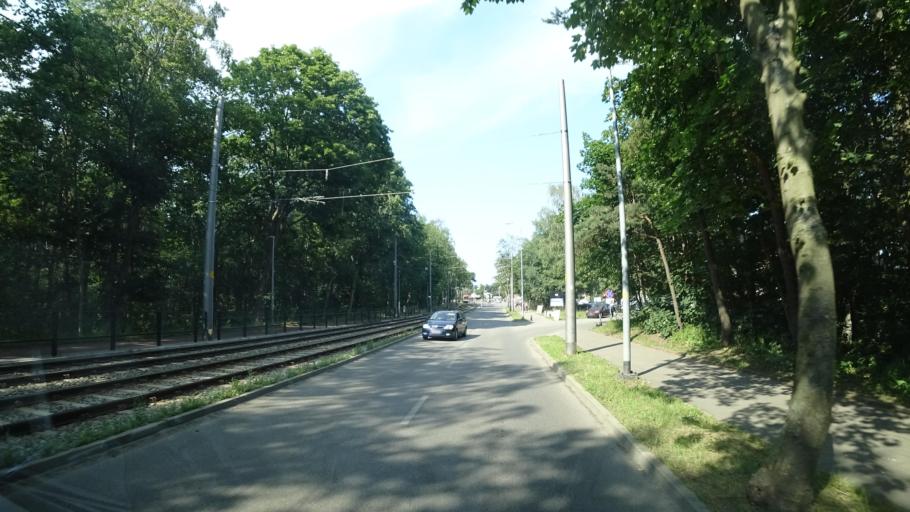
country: PL
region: Pomeranian Voivodeship
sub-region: Gdansk
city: Gdansk
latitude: 54.3707
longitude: 18.7273
